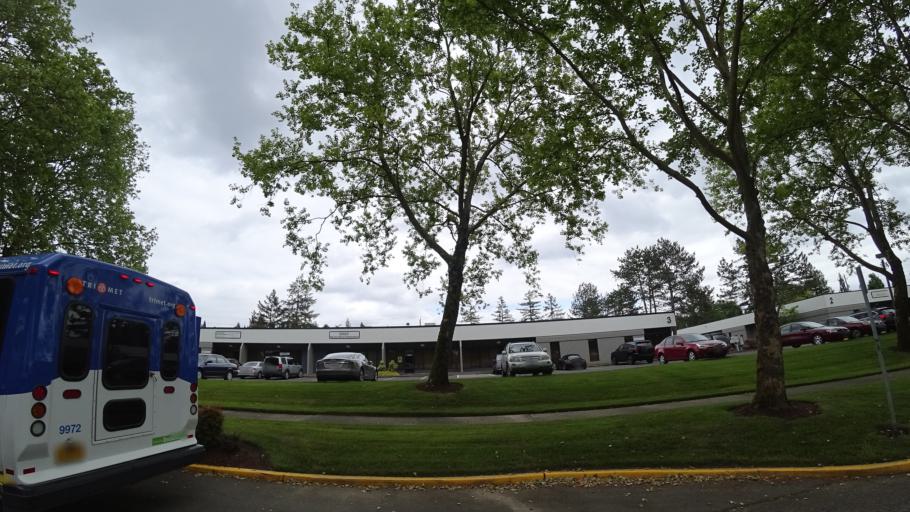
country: US
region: Oregon
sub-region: Washington County
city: Garden Home-Whitford
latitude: 45.4602
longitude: -122.7892
